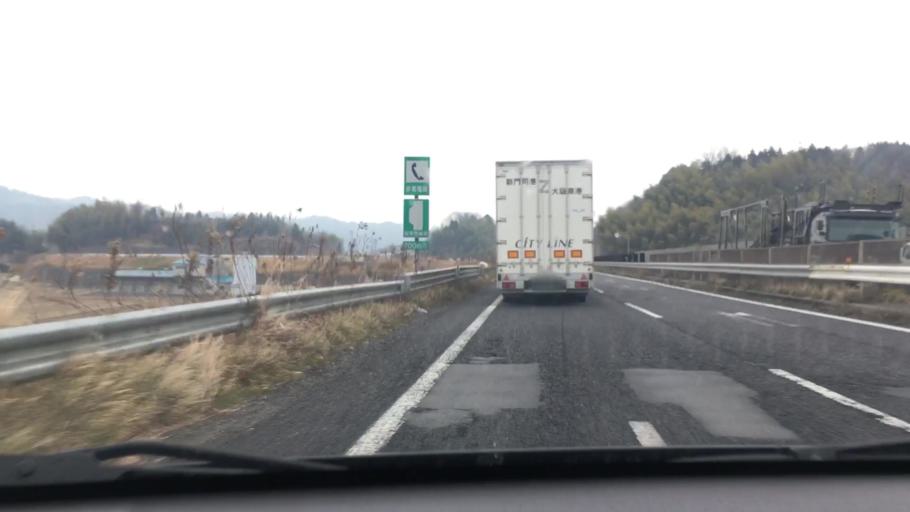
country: JP
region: Mie
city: Ueno-ebisumachi
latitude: 34.7822
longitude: 136.1587
